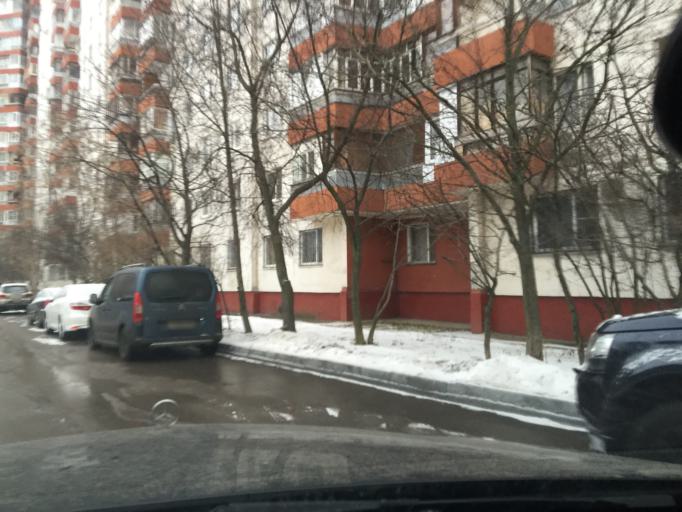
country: RU
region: Moscow
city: Troparevo
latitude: 55.6420
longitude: 37.4767
